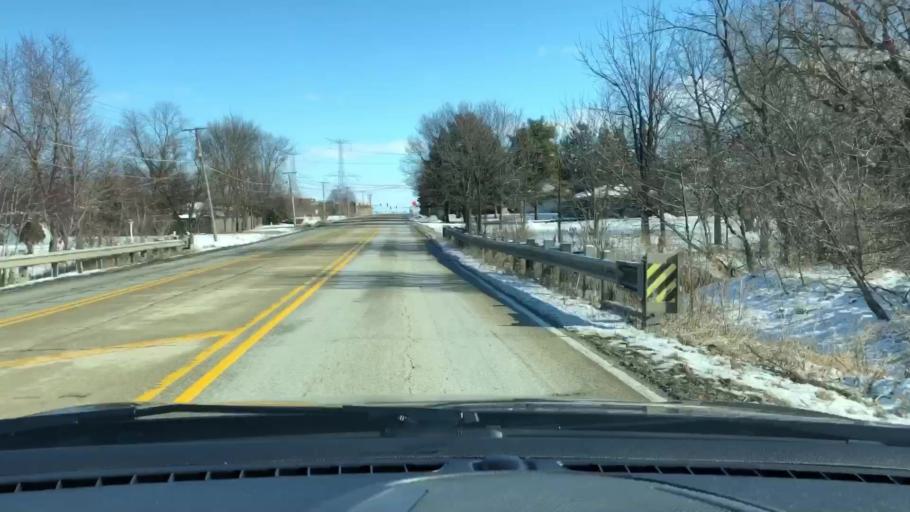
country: US
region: Illinois
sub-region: Will County
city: Ingalls Park
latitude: 41.4818
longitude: -88.0355
